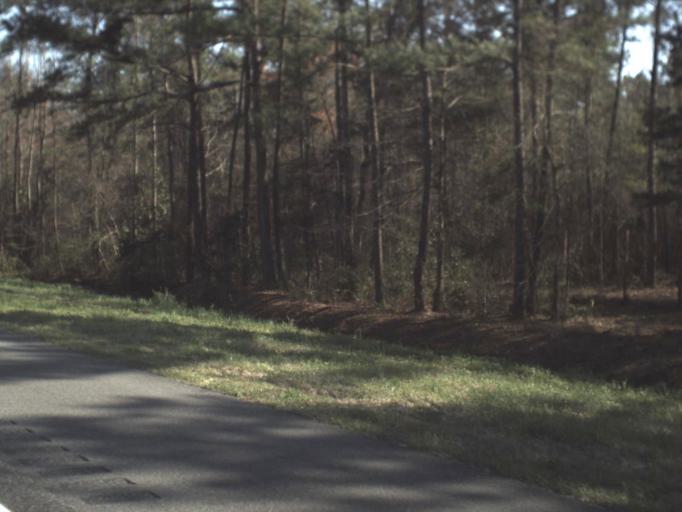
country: US
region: Florida
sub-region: Gadsden County
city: Midway
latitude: 30.5182
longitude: -84.4851
